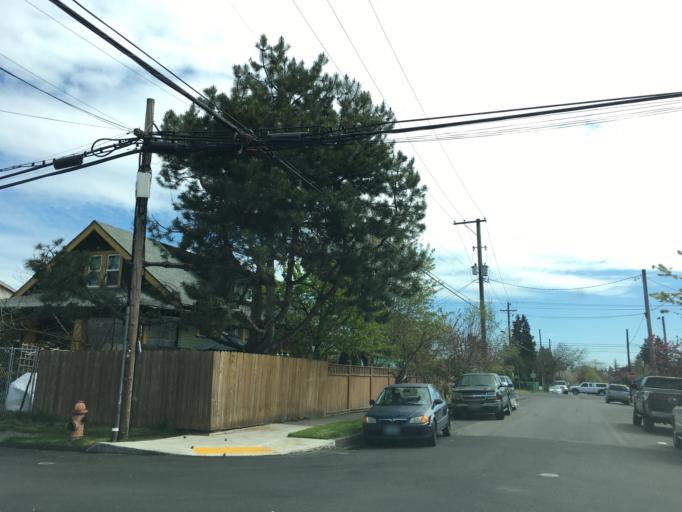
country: US
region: Oregon
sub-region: Multnomah County
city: Lents
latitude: 45.5302
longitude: -122.5801
